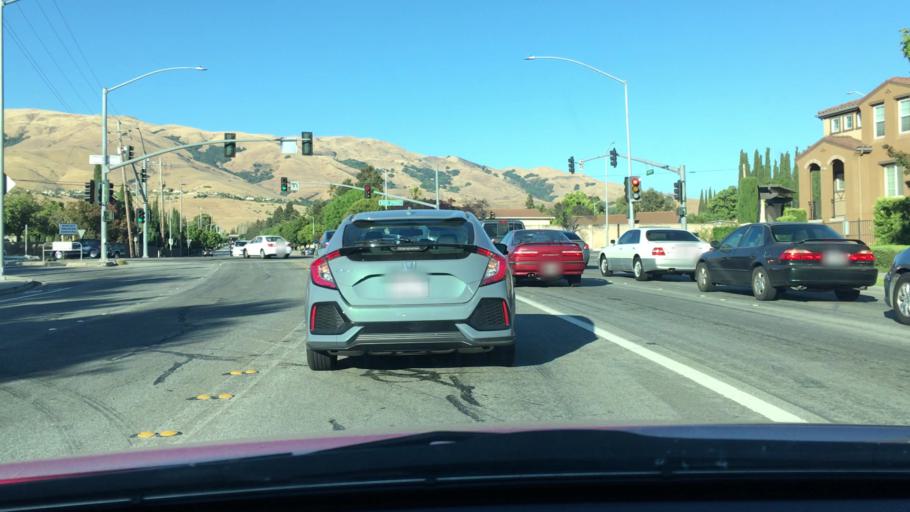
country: US
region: California
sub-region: Santa Clara County
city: Milpitas
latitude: 37.4633
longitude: -121.9150
